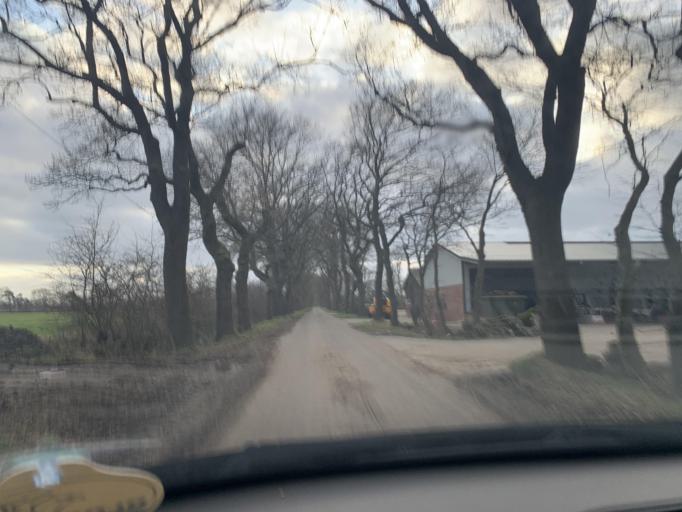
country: DE
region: Lower Saxony
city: Westerstede
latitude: 53.2989
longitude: 7.9321
